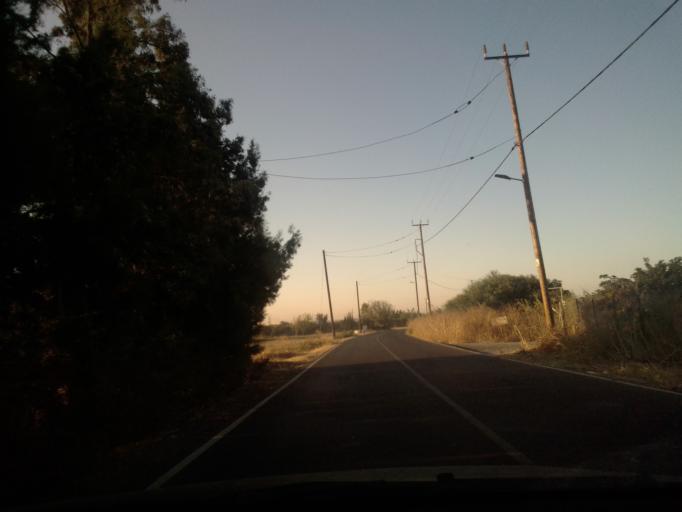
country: CY
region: Limassol
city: Ypsonas
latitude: 34.6734
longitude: 32.9587
